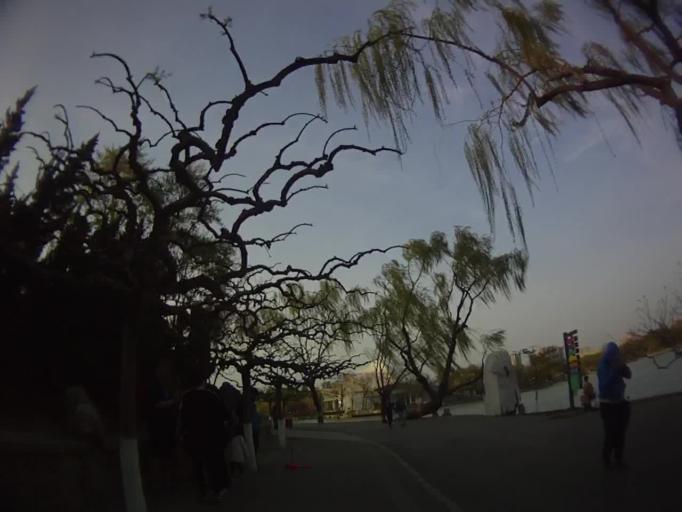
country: CN
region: Beijing
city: Longtan
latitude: 39.8763
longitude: 116.4326
